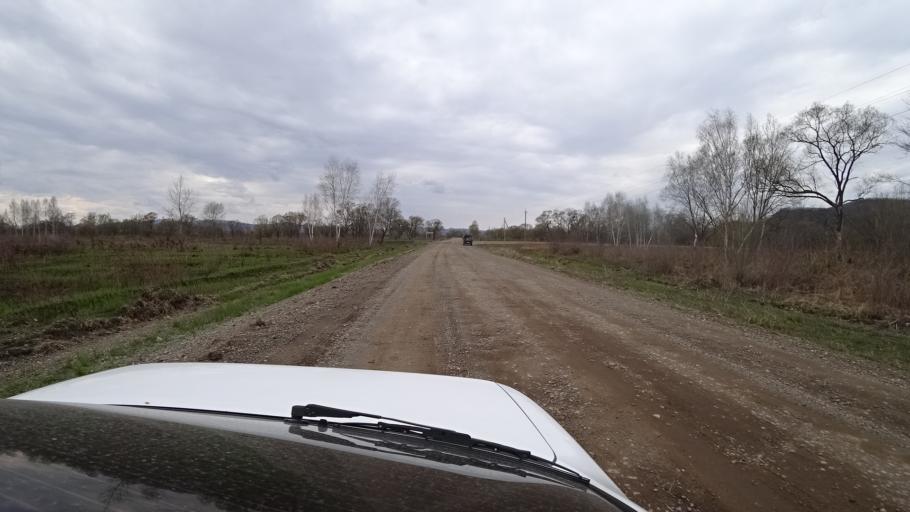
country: RU
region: Primorskiy
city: Novopokrovka
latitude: 45.5611
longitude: 134.3382
